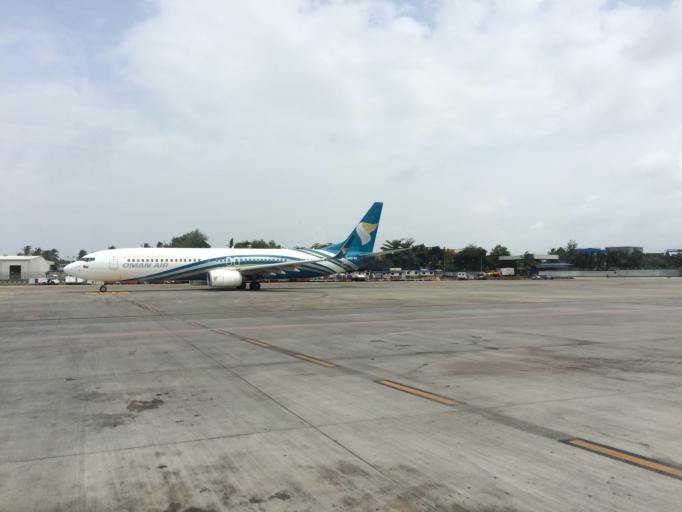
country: IN
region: Maharashtra
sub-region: Mumbai Suburban
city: Mumbai
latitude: 19.0955
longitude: 72.8712
